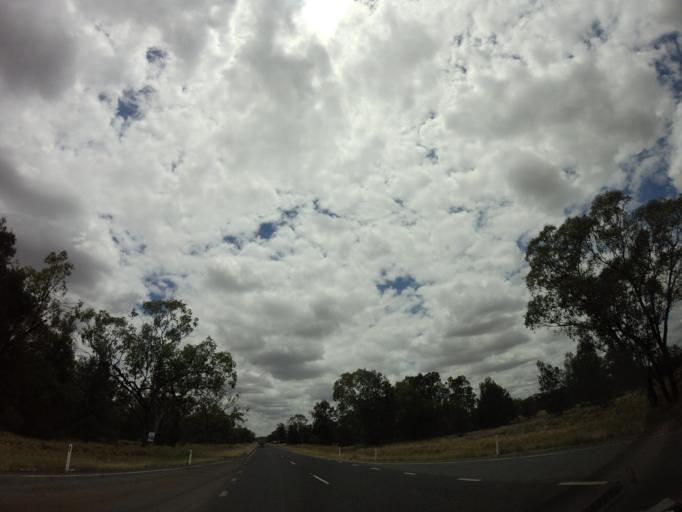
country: AU
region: Queensland
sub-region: Goondiwindi
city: Goondiwindi
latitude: -28.4533
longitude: 150.2979
